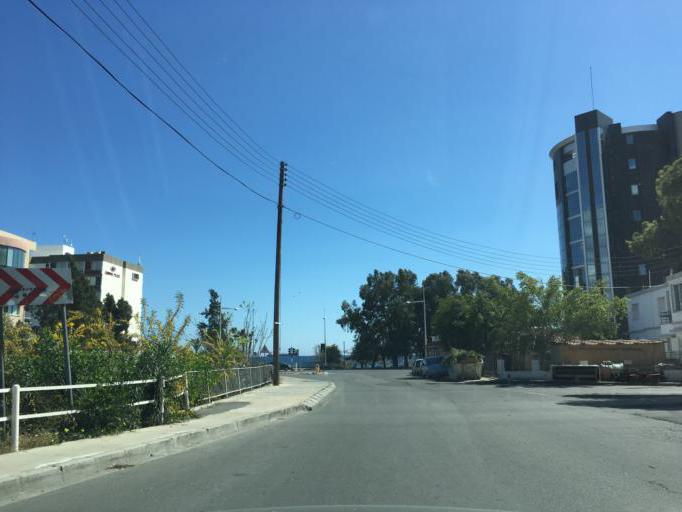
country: CY
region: Limassol
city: Limassol
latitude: 34.6897
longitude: 33.0697
